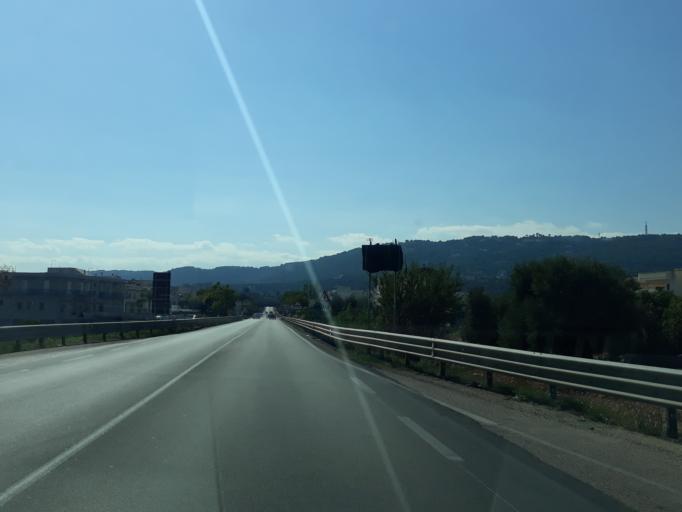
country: IT
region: Apulia
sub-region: Provincia di Brindisi
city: Fasano
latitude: 40.8455
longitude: 17.3548
